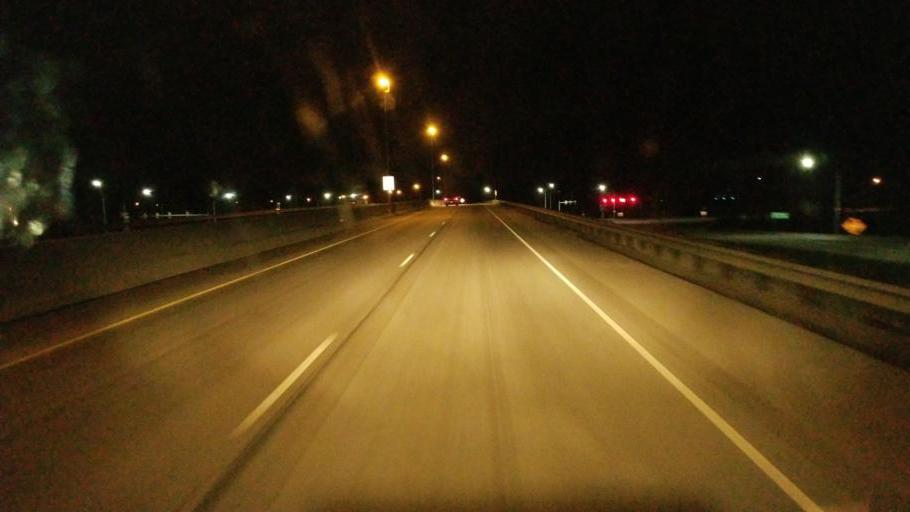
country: US
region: Ohio
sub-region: Licking County
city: Newark
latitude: 40.0623
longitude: -82.4276
